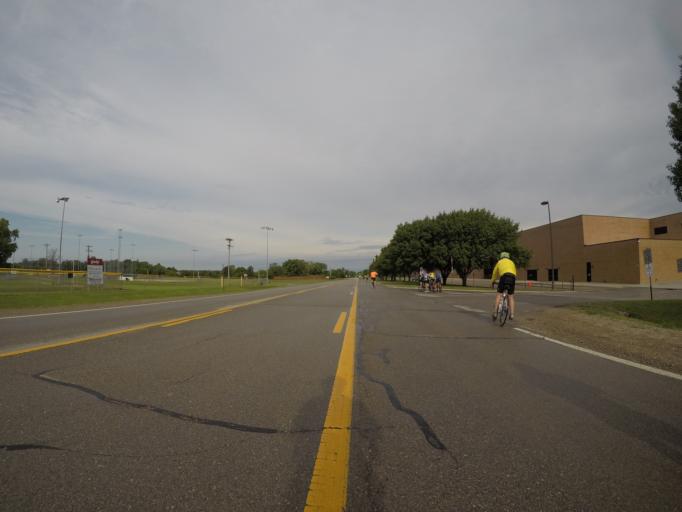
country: US
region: Kansas
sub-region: Shawnee County
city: Auburn
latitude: 38.9565
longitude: -95.7584
